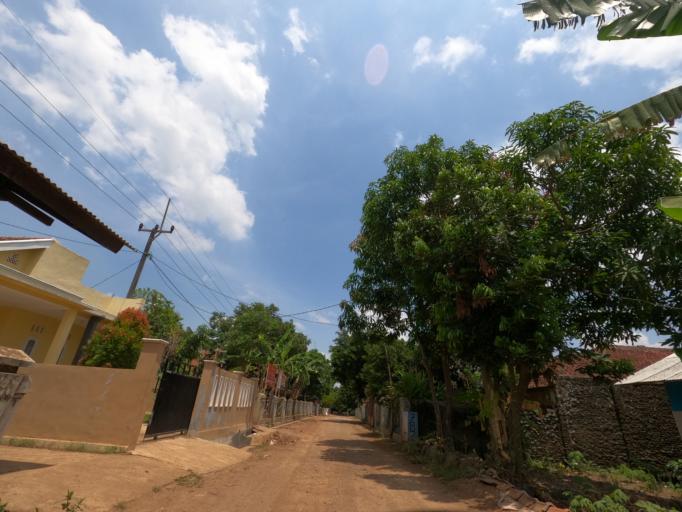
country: ID
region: West Java
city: Pamanukan
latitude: -6.5142
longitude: 107.7723
